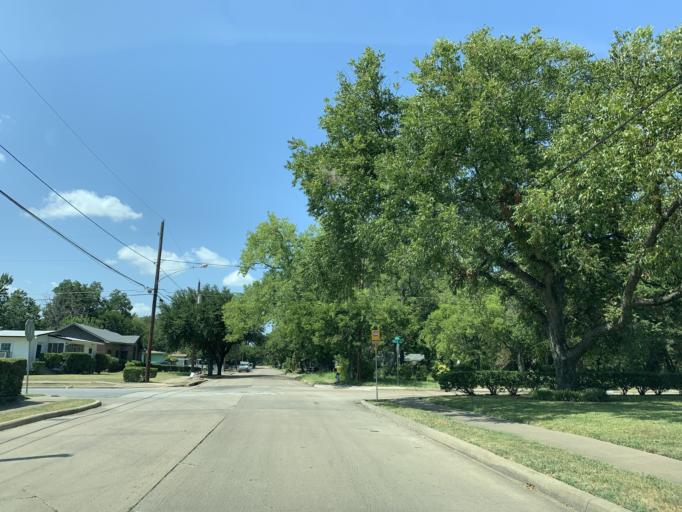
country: US
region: Texas
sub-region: Dallas County
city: Hutchins
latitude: 32.7024
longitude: -96.7645
